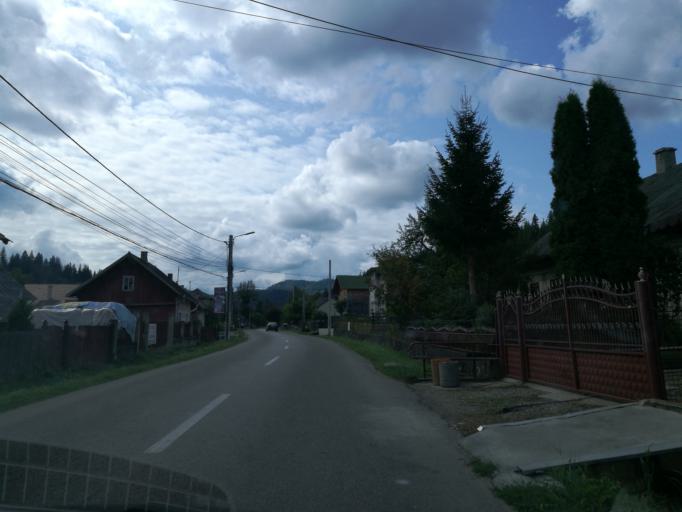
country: RO
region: Suceava
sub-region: Oras Gura Humorului
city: Gura Humorului
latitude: 47.5329
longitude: 25.8643
